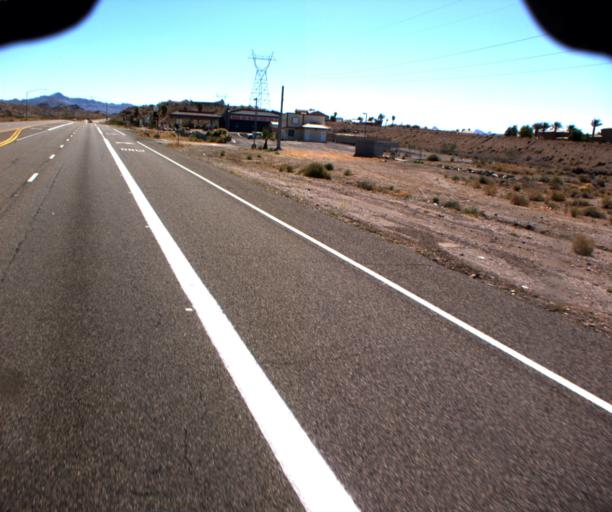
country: US
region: Nevada
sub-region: Clark County
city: Laughlin
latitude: 35.1904
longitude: -114.5300
